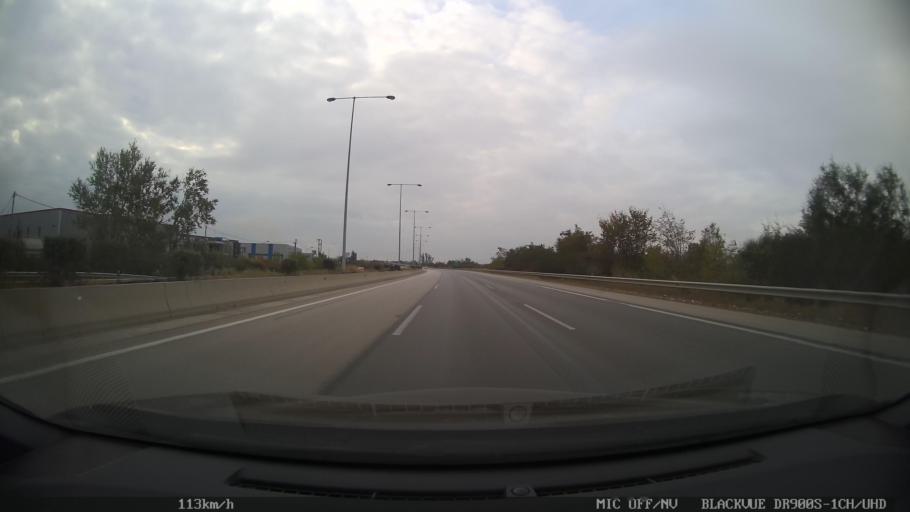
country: GR
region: Central Macedonia
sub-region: Nomos Thessalonikis
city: Nea Magnisia
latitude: 40.6769
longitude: 22.8323
